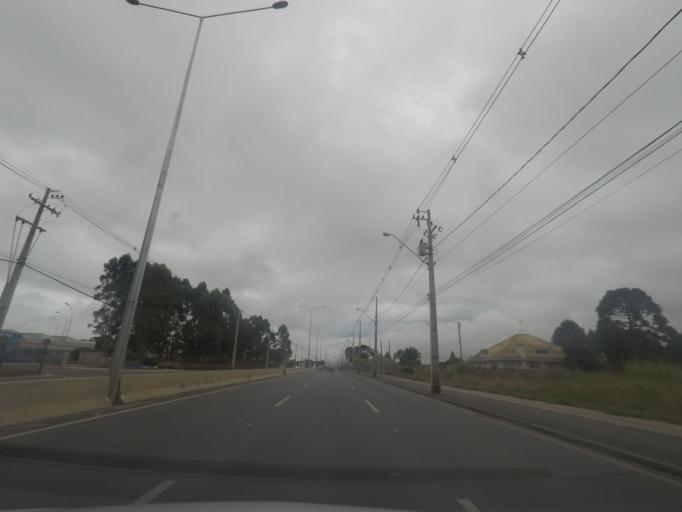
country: BR
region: Parana
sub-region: Piraquara
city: Piraquara
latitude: -25.4592
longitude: -49.0974
